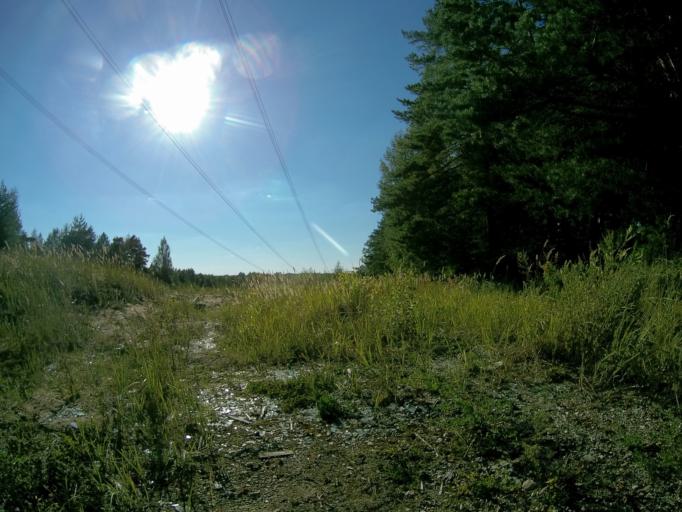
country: RU
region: Vladimir
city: Kommunar
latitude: 56.0623
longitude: 40.4324
